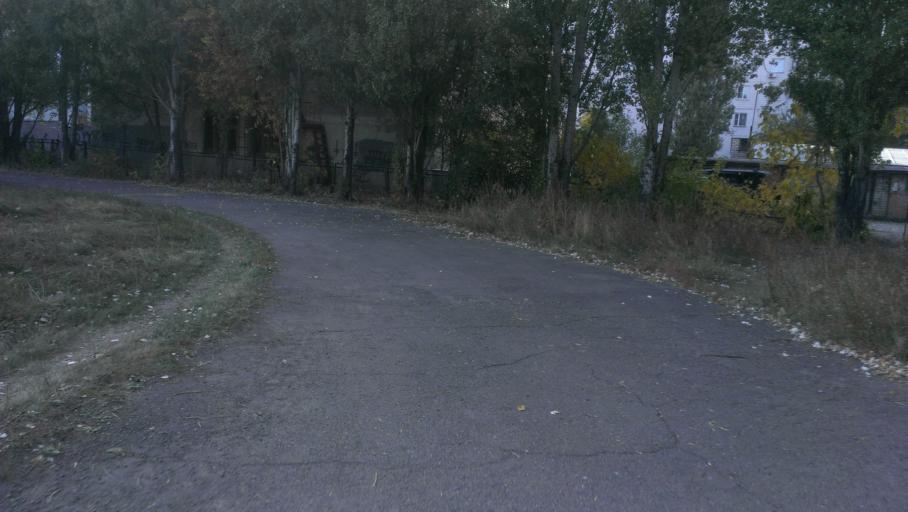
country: RU
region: Altai Krai
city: Novosilikatnyy
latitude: 53.3341
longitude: 83.6707
